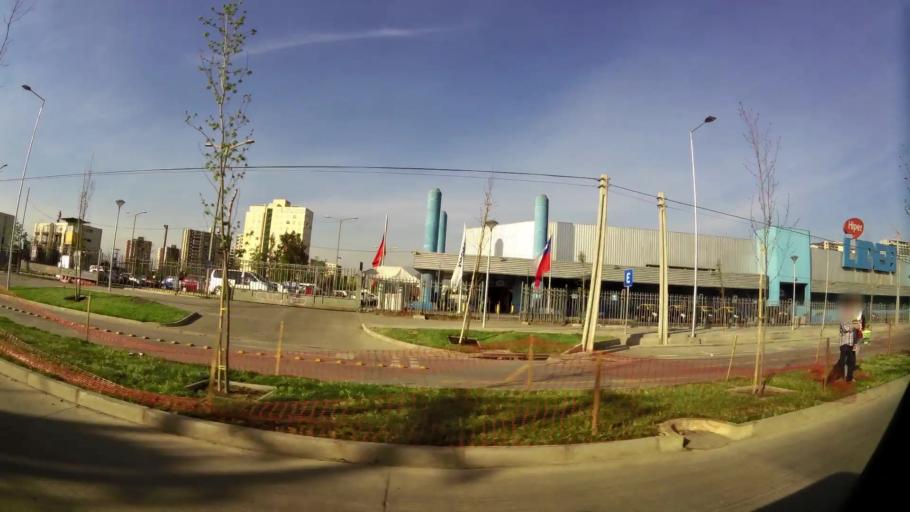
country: CL
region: Santiago Metropolitan
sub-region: Provincia de Santiago
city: Villa Presidente Frei, Nunoa, Santiago, Chile
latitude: -33.5194
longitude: -70.6030
